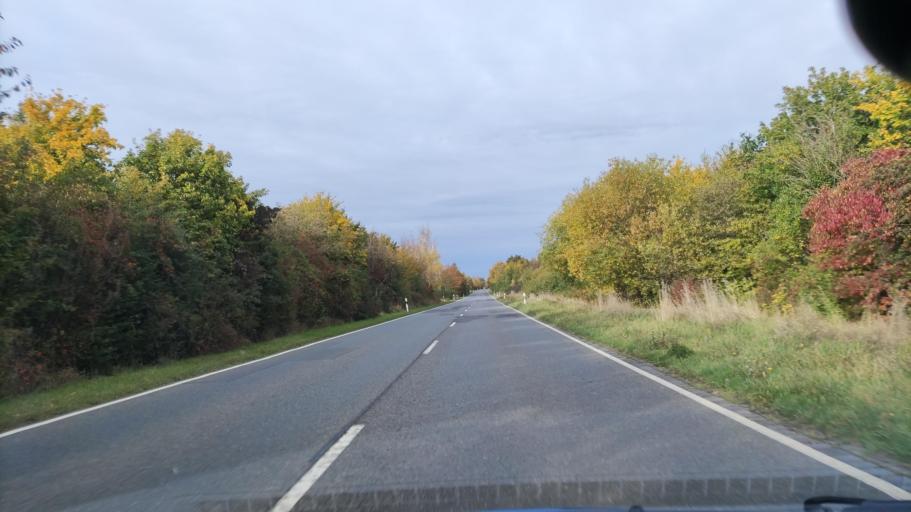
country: DE
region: Saxony-Anhalt
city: Darlingerode
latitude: 51.8591
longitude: 10.7544
